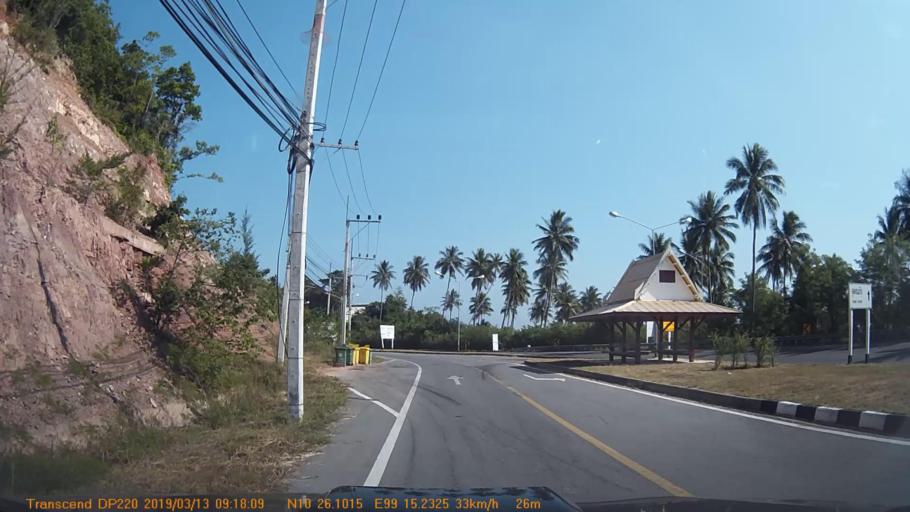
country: TH
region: Chumphon
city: Chumphon
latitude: 10.4353
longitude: 99.2539
